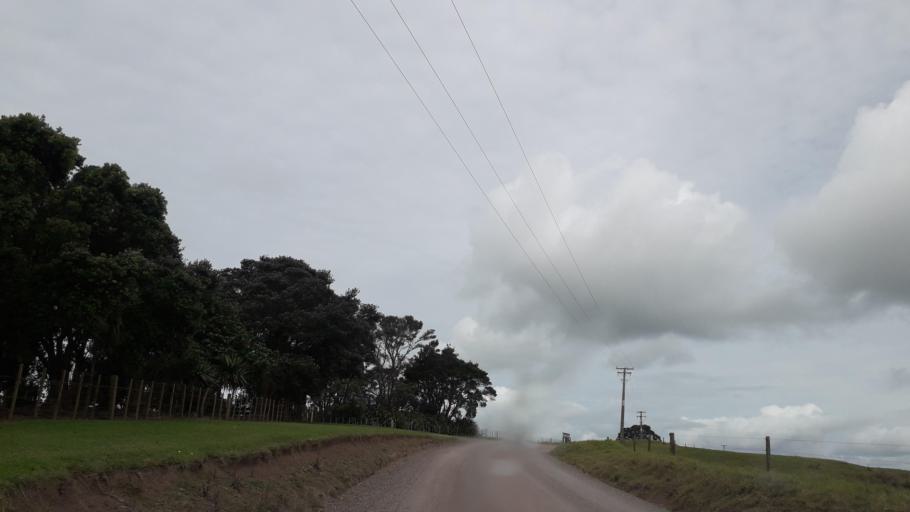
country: NZ
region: Northland
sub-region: Far North District
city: Kerikeri
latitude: -35.1308
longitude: 174.0133
